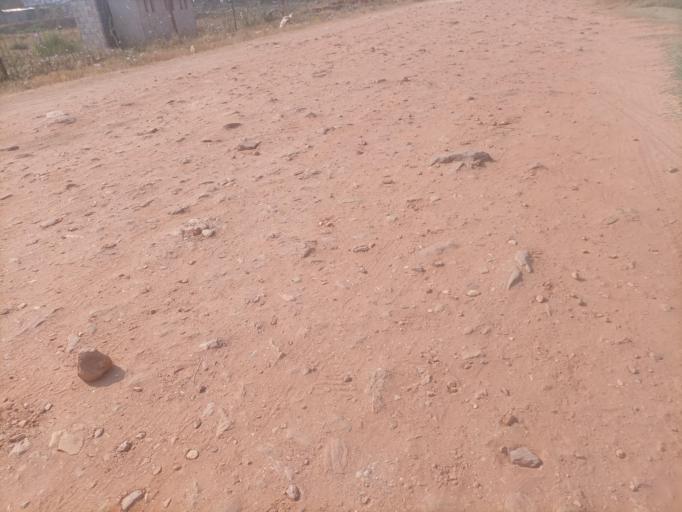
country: ZM
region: Lusaka
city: Lusaka
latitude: -15.3979
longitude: 28.3939
